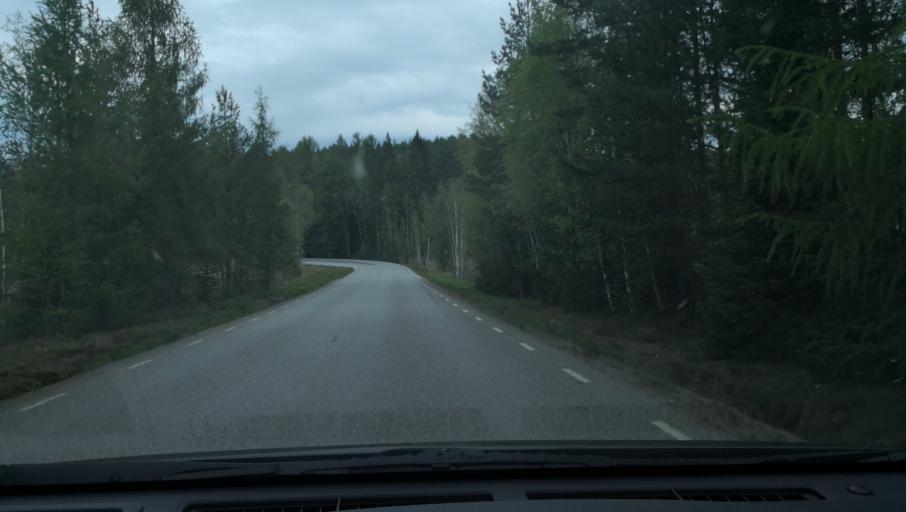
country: SE
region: Vaestmanland
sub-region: Skinnskattebergs Kommun
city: Skinnskatteberg
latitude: 59.8308
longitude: 15.5772
